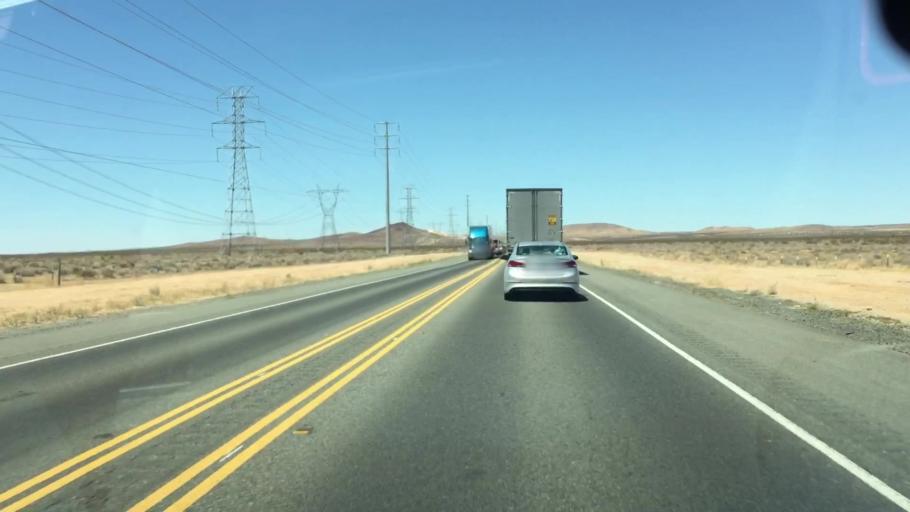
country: US
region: California
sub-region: Kern County
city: Boron
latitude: 34.8361
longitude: -117.4983
